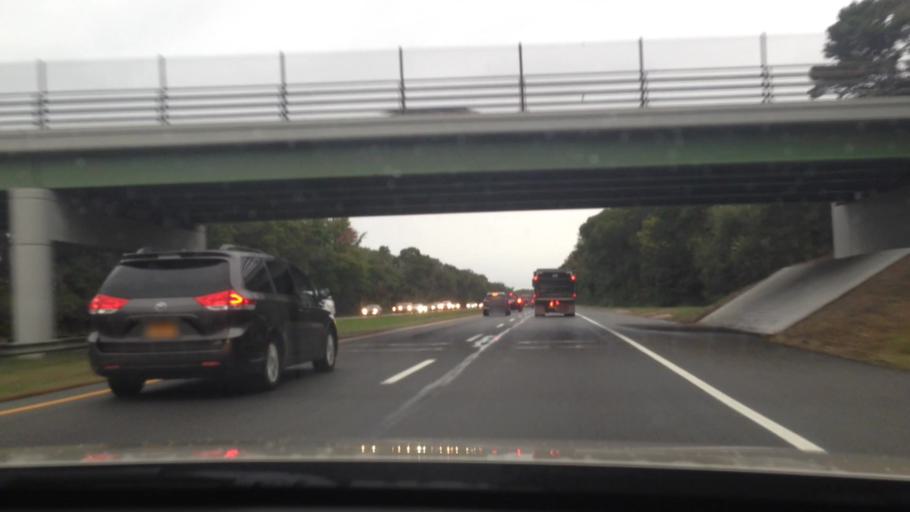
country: US
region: New York
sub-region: Suffolk County
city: Holtsville
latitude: 40.8258
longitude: -73.0548
